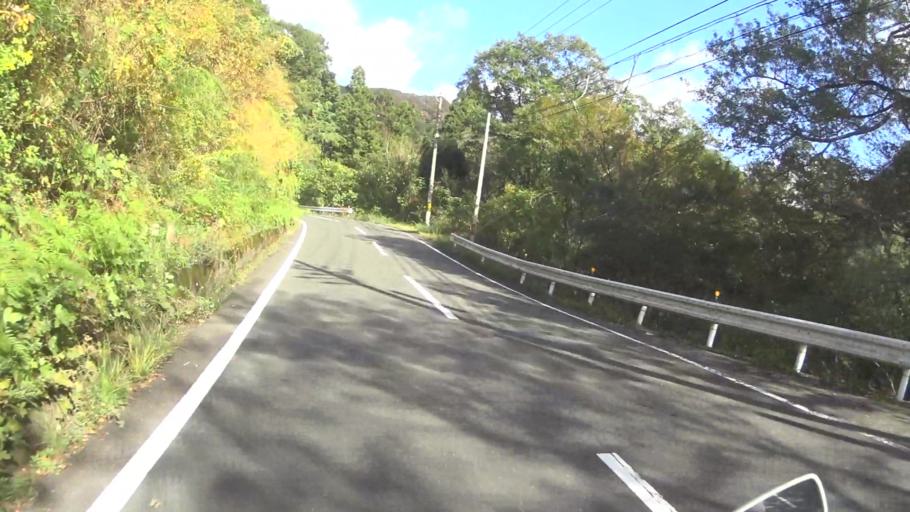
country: JP
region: Kyoto
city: Maizuru
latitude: 35.5357
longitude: 135.4440
